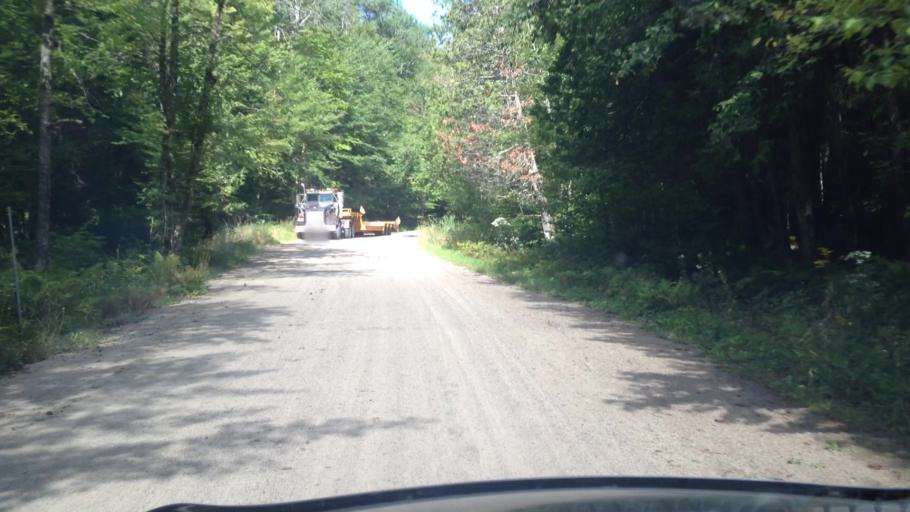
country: CA
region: Quebec
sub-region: Laurentides
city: Mont-Tremblant
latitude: 45.9233
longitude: -74.5819
